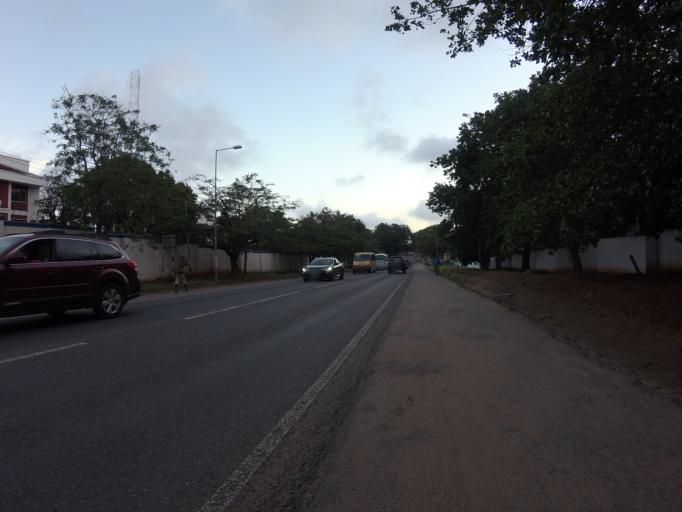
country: GH
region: Greater Accra
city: Accra
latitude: 5.5717
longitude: -0.1843
